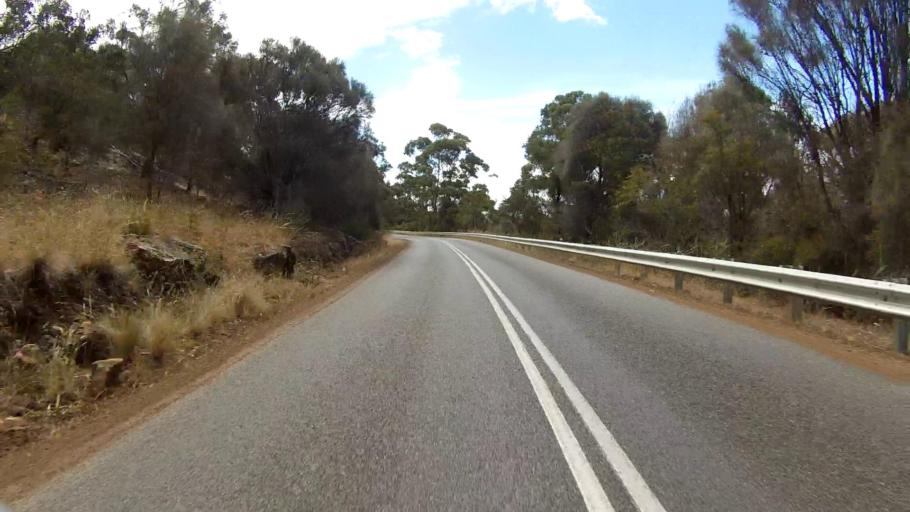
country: AU
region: Tasmania
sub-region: Sorell
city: Sorell
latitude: -42.2242
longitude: 148.0290
